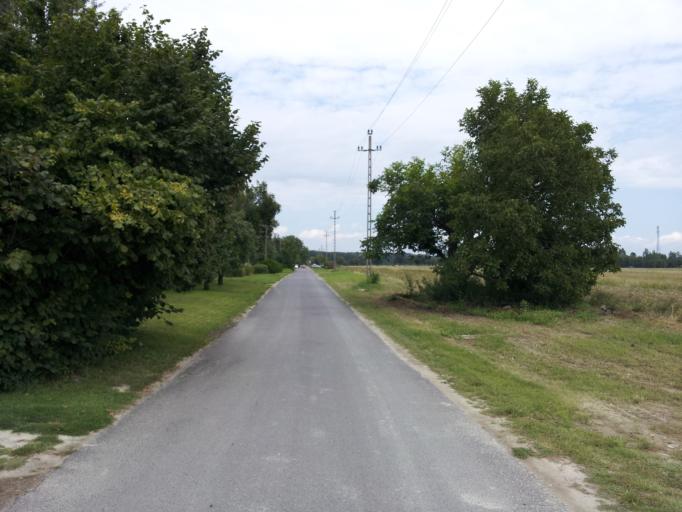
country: HU
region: Pest
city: Rackeve
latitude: 47.1898
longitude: 18.9597
